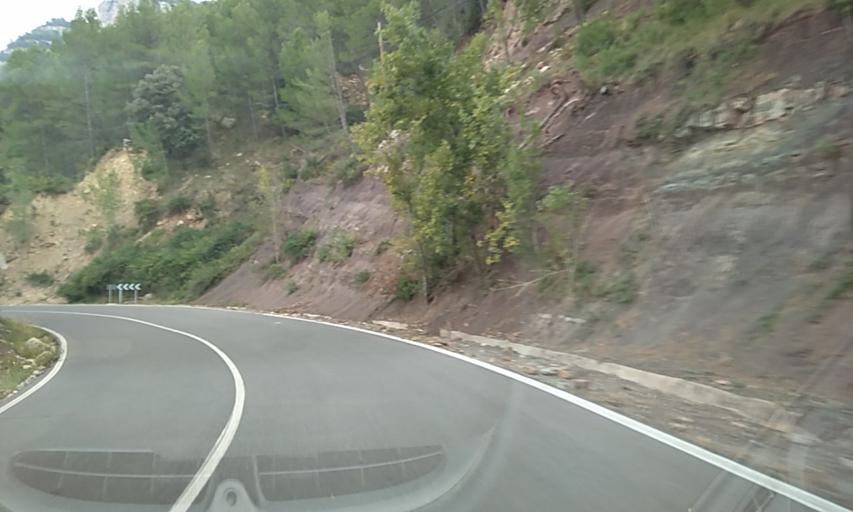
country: ES
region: Valencia
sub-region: Provincia de Castello
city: Puebla de Arenoso
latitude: 40.0854
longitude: -0.5550
